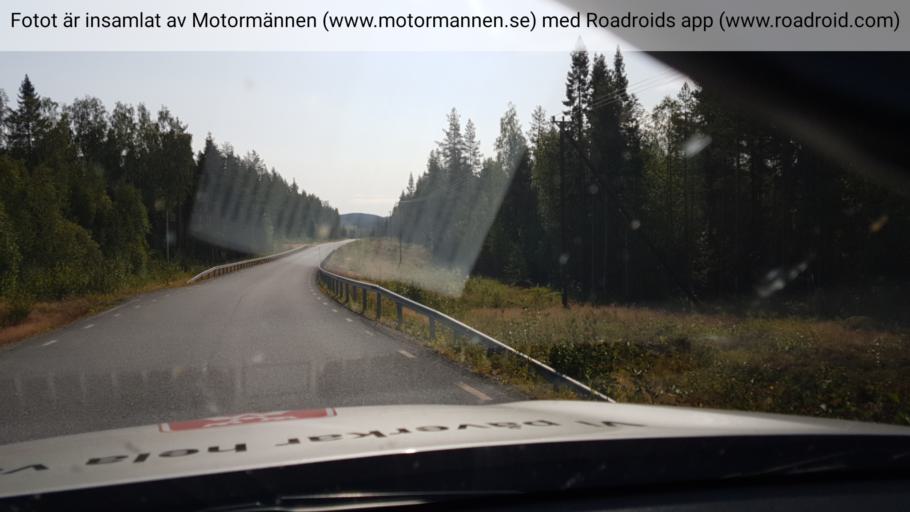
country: SE
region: Norrbotten
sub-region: Alvsbyns Kommun
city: AElvsbyn
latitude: 65.5873
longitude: 20.6820
